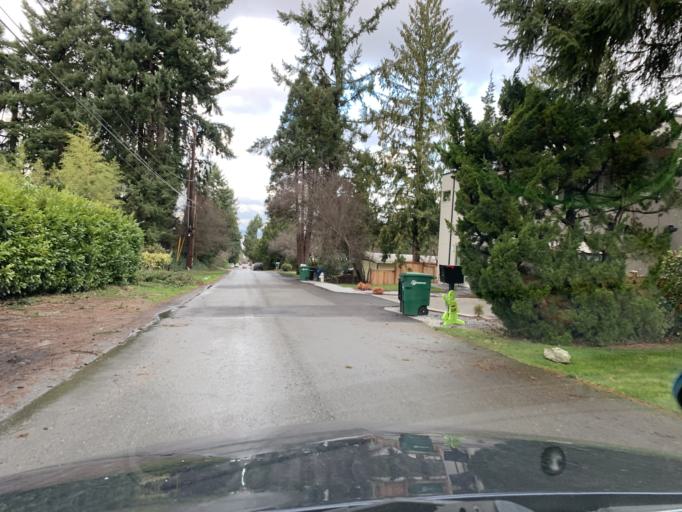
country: US
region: Washington
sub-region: King County
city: Mercer Island
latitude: 47.5857
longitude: -122.2441
